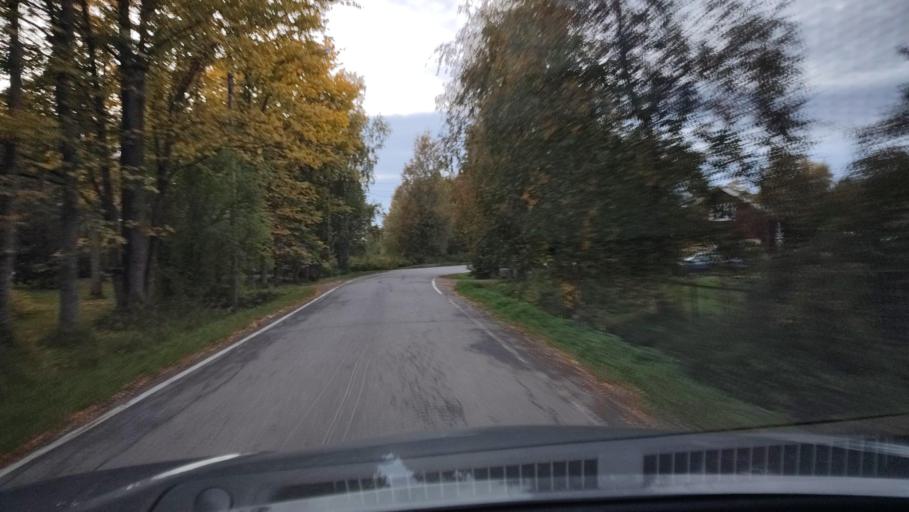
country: FI
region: Ostrobothnia
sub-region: Sydosterbotten
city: Kristinestad
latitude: 62.2574
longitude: 21.5092
